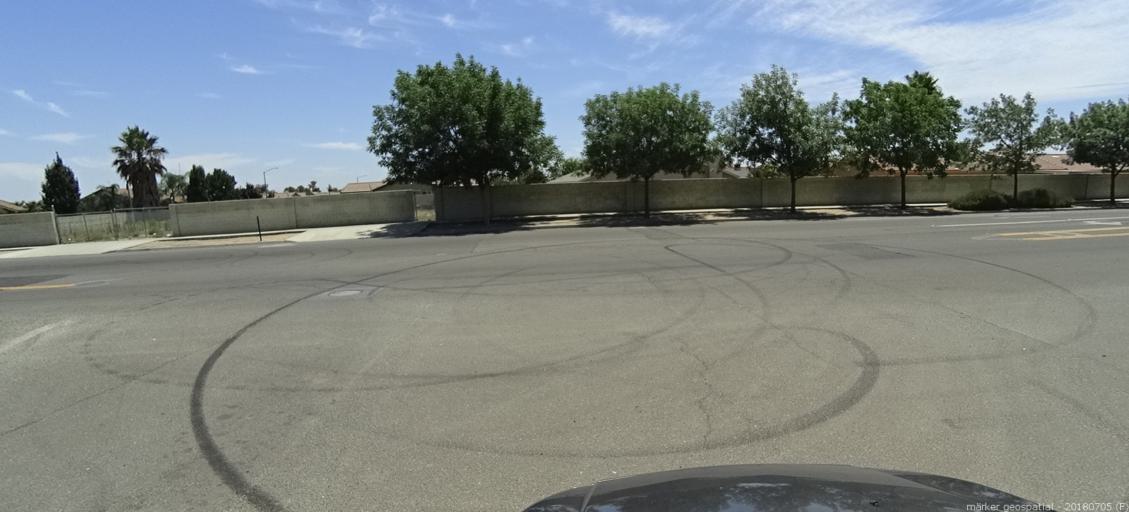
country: US
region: California
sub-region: Madera County
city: Madera
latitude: 36.9869
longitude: -120.0452
